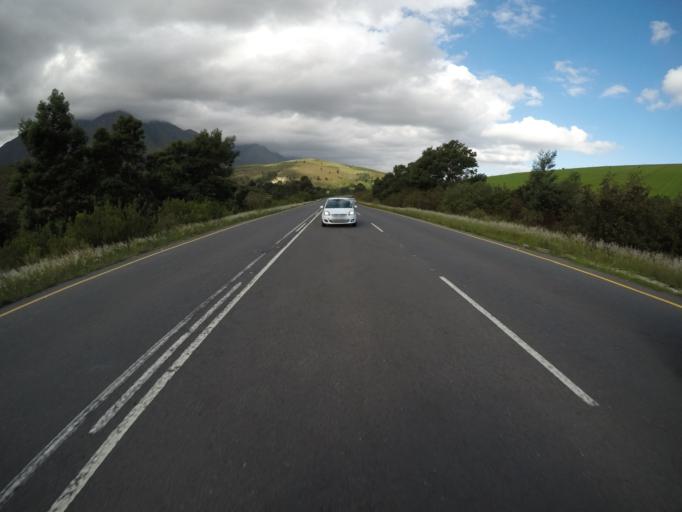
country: ZA
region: Western Cape
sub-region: Overberg District Municipality
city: Swellendam
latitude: -33.9998
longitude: 20.3649
